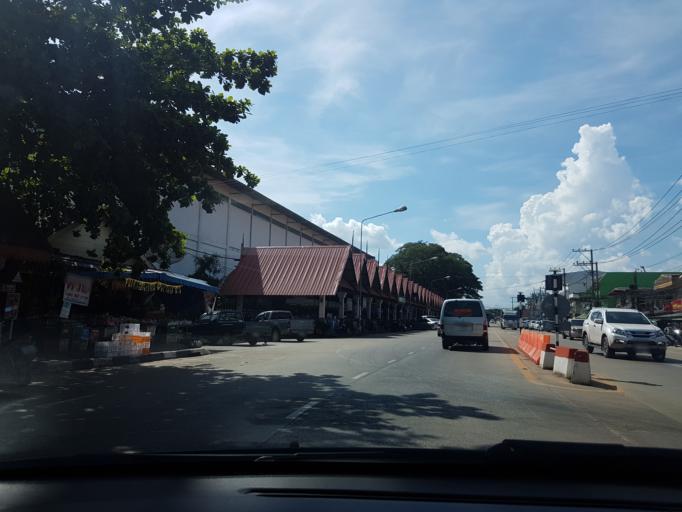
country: TH
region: Lampang
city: Ko Kha
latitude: 18.1922
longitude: 99.4002
